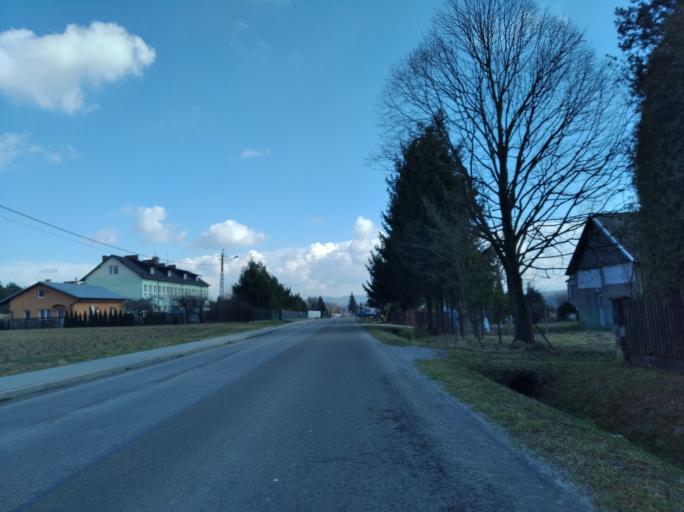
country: PL
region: Subcarpathian Voivodeship
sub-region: Powiat strzyzowski
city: Frysztak
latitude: 49.8486
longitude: 21.5421
